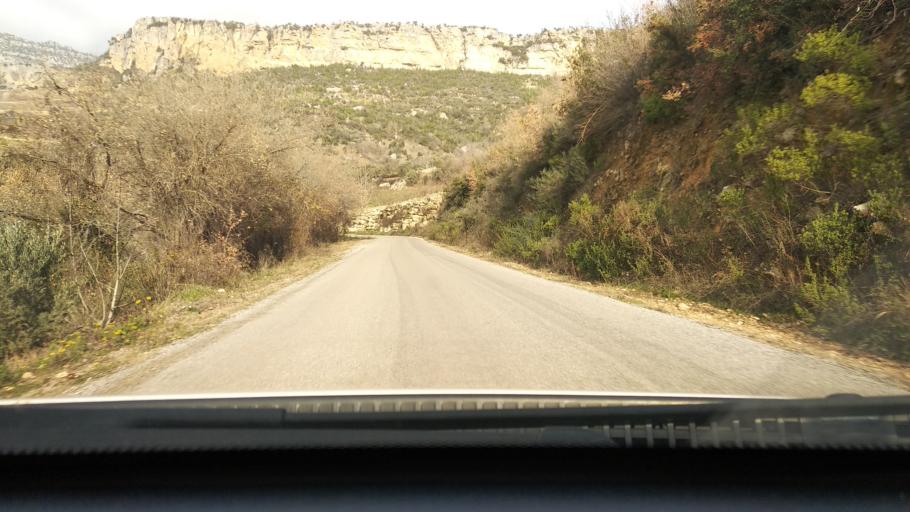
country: TR
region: Mersin
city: Kuzucubelen
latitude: 36.8679
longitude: 34.4699
